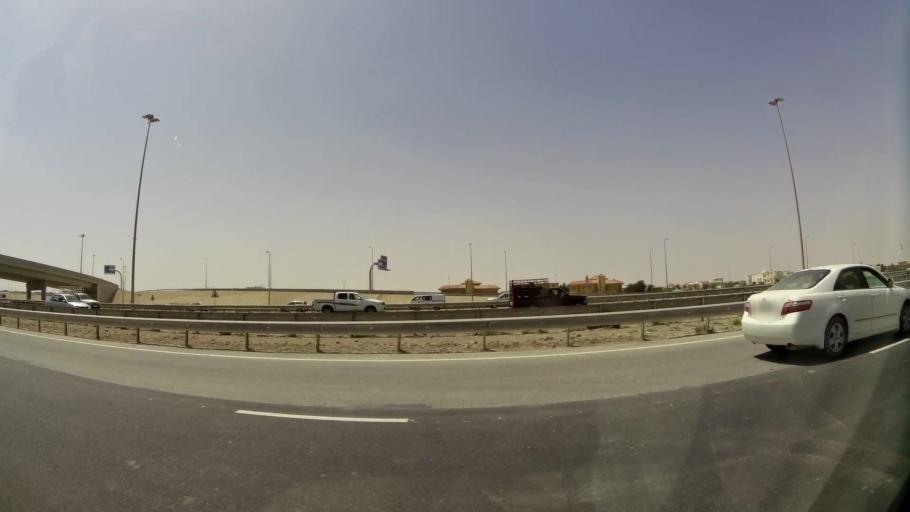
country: QA
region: Baladiyat Umm Salal
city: Umm Salal Muhammad
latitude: 25.3823
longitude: 51.4394
